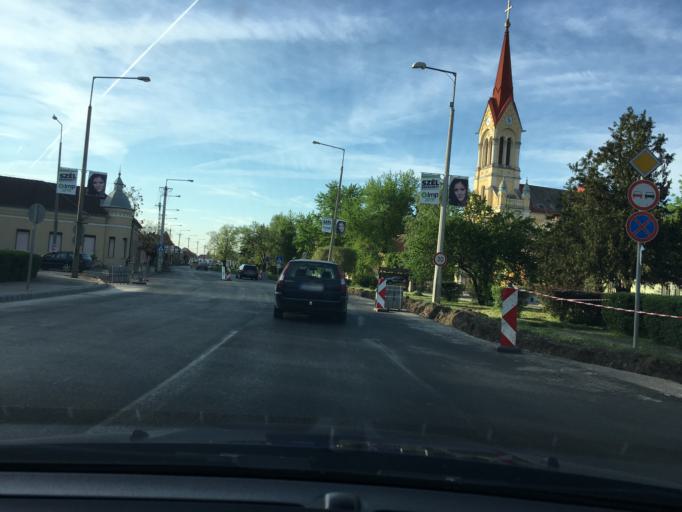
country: HU
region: Hajdu-Bihar
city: Berettyoujfalu
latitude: 47.2259
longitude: 21.5350
